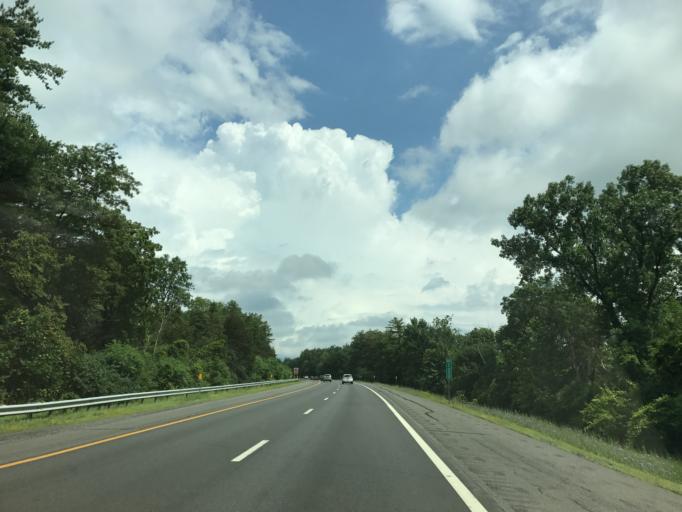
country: US
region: New York
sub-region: Greene County
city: Coxsackie
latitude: 42.3343
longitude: -73.8596
